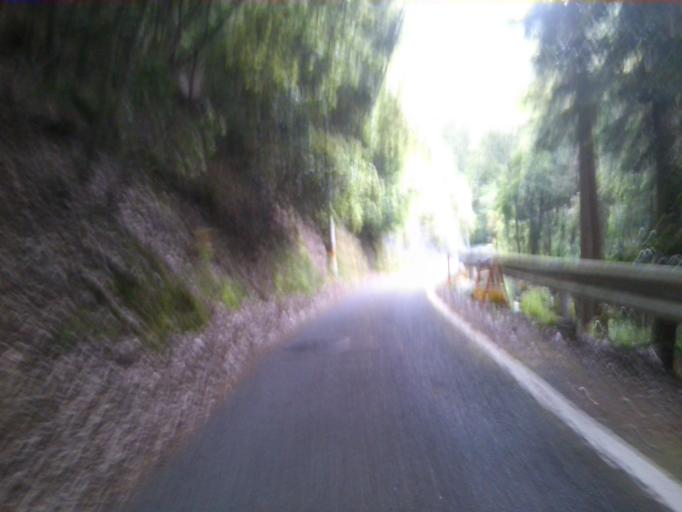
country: JP
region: Kyoto
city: Muko
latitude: 34.9538
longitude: 135.6444
